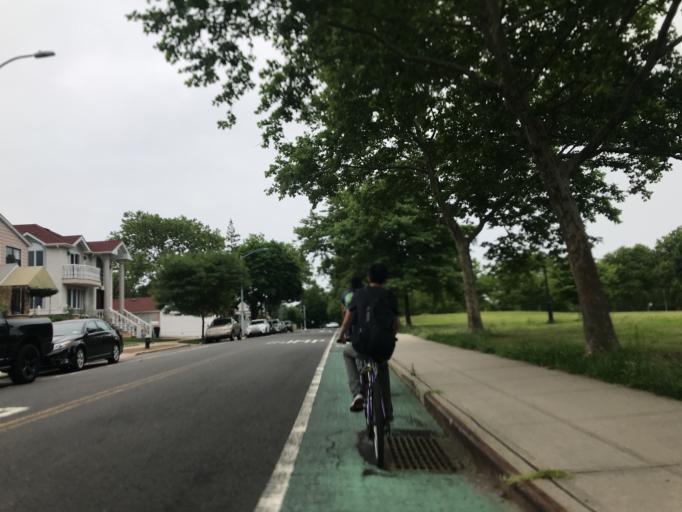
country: US
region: New York
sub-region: Queens County
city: Jamaica
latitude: 40.7444
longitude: -73.7848
